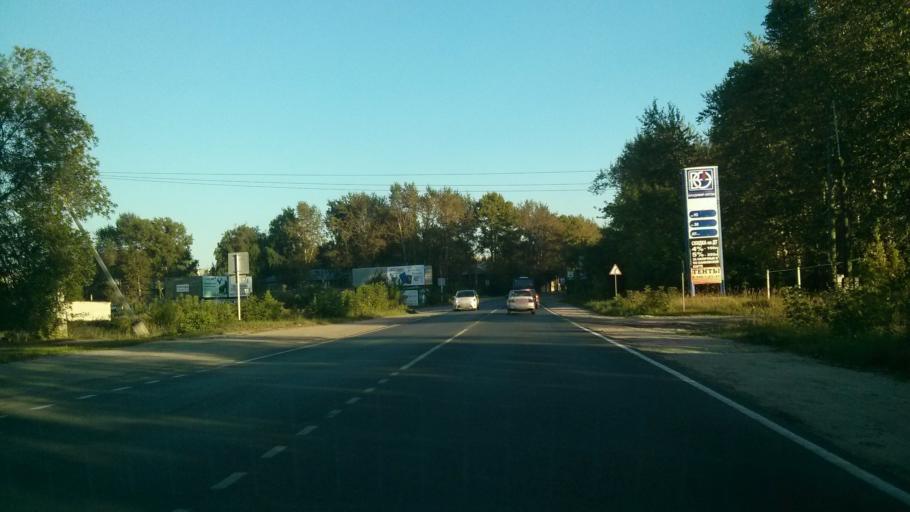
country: RU
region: Vladimir
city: Murom
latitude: 55.5987
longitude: 42.0324
